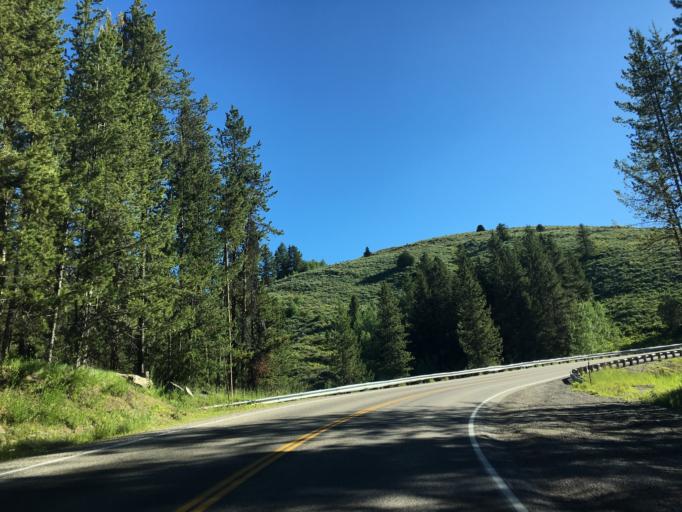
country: US
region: Idaho
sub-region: Teton County
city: Victor
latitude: 43.5714
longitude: -111.2416
